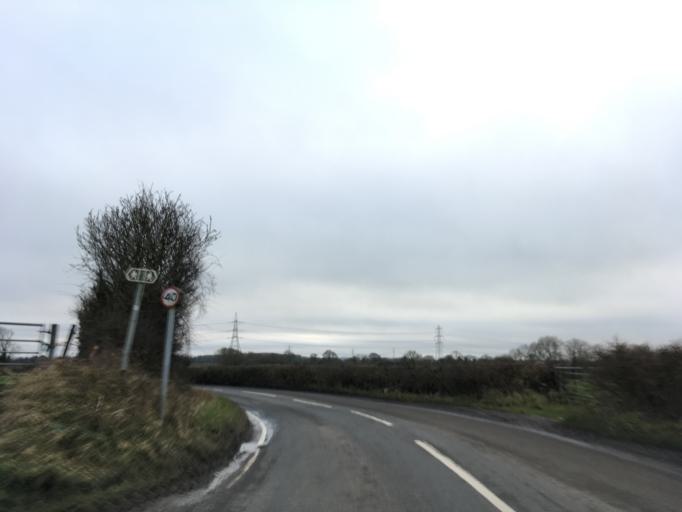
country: GB
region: England
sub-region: South Gloucestershire
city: Alveston
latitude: 51.5619
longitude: -2.5103
